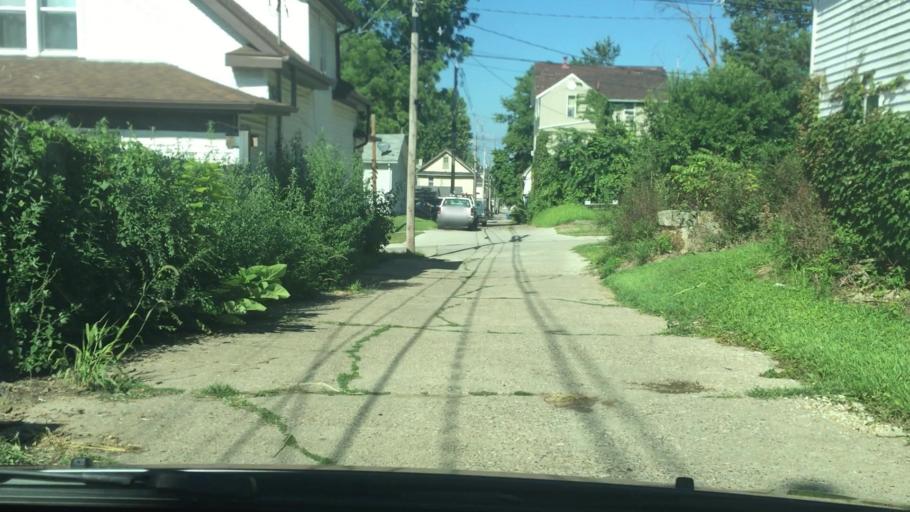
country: US
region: Iowa
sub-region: Muscatine County
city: Muscatine
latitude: 41.4207
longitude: -91.0523
